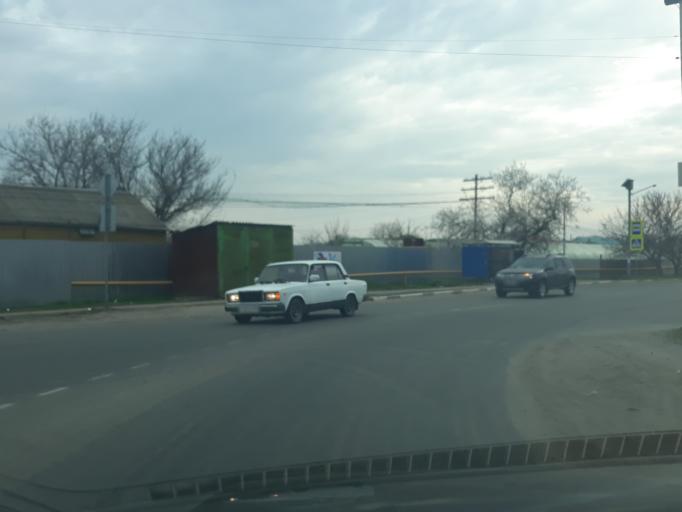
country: RU
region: Rostov
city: Novobessergenovka
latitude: 47.1821
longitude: 38.8196
